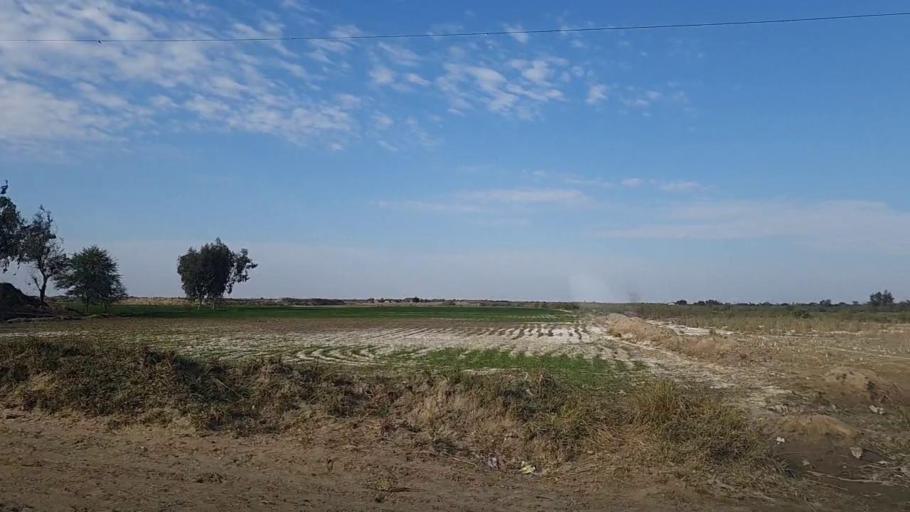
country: PK
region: Sindh
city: Jam Sahib
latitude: 26.3167
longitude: 68.8080
